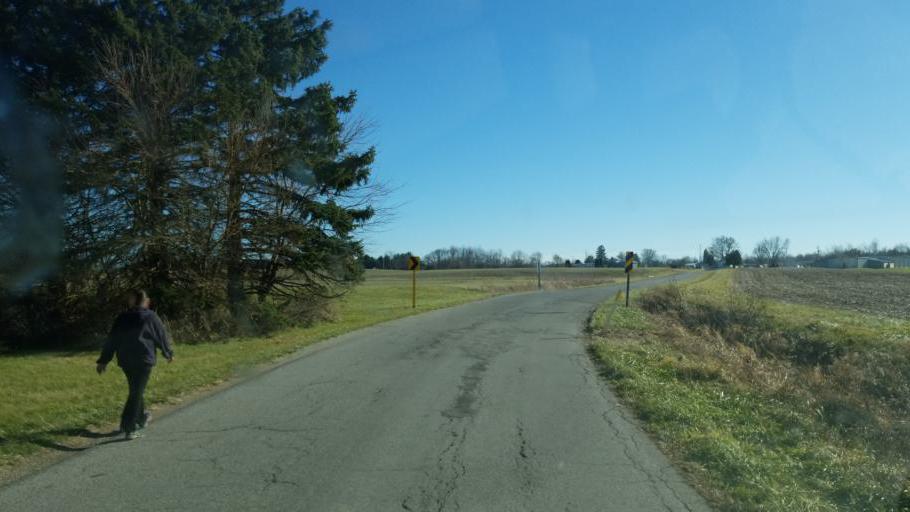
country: US
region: Ohio
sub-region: Crawford County
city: Galion
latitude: 40.6652
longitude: -82.8400
